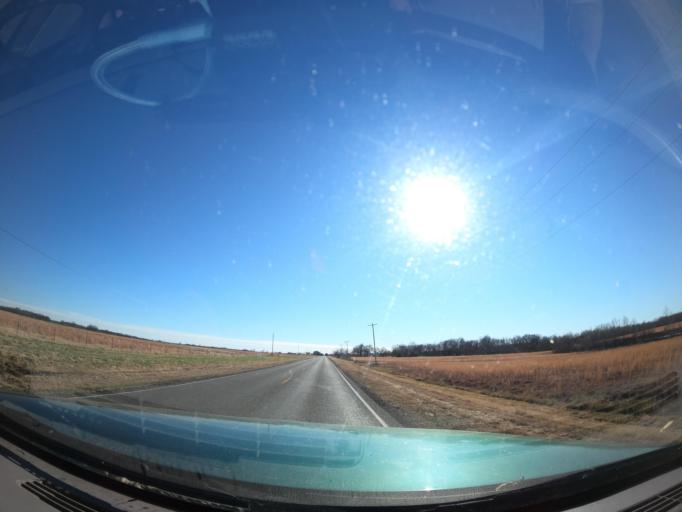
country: US
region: Oklahoma
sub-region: Muskogee County
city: Haskell
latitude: 35.6749
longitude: -95.6423
